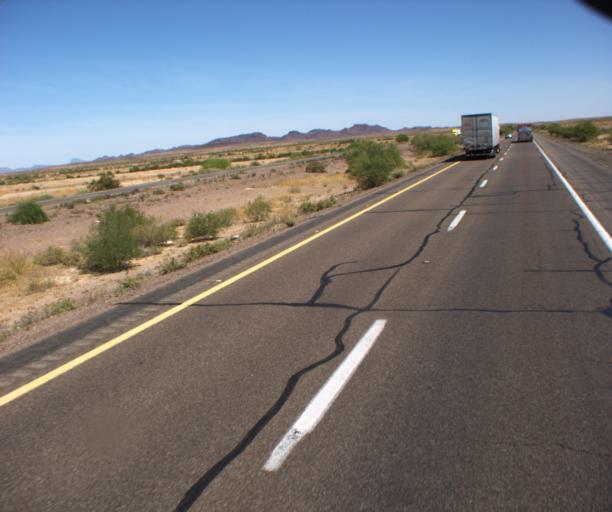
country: US
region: Arizona
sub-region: Maricopa County
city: Gila Bend
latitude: 32.8823
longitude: -113.0968
